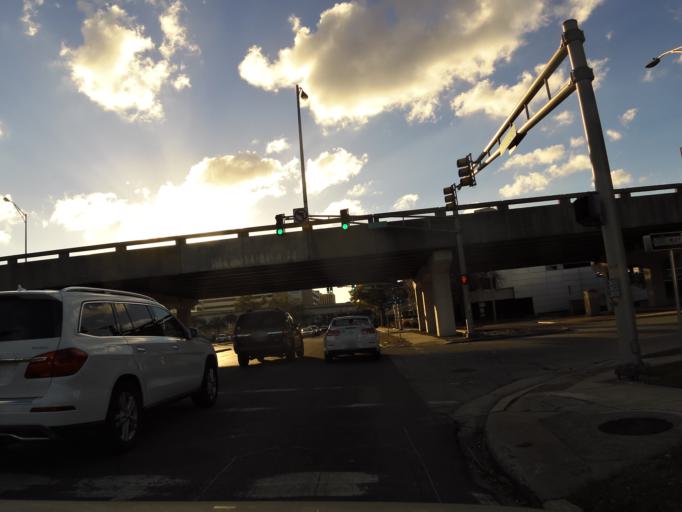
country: US
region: Florida
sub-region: Duval County
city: Jacksonville
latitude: 30.3071
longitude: -81.6579
